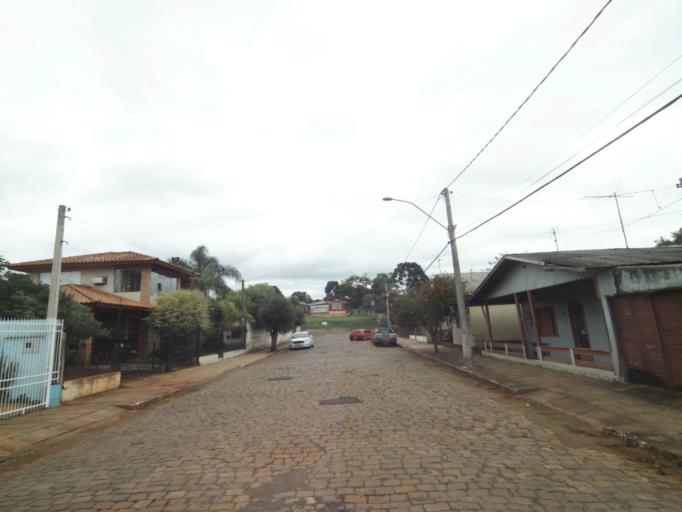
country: BR
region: Rio Grande do Sul
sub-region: Lagoa Vermelha
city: Lagoa Vermelha
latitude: -28.2089
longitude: -51.5309
